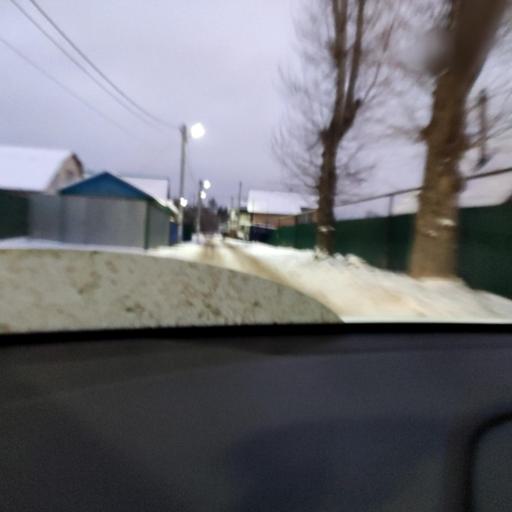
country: RU
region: Tatarstan
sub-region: Gorod Kazan'
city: Kazan
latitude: 55.8803
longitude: 49.0787
